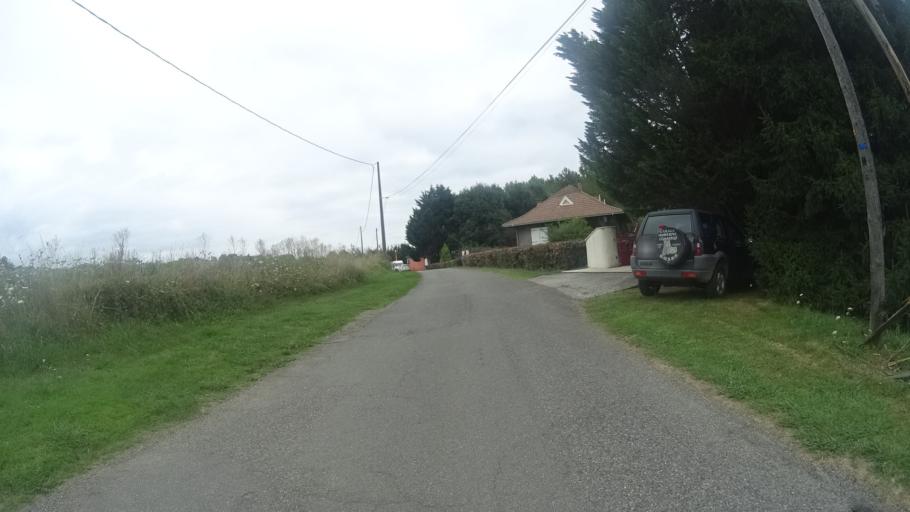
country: FR
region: Aquitaine
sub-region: Departement des Pyrenees-Atlantiques
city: Mont
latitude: 43.4863
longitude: -0.6969
